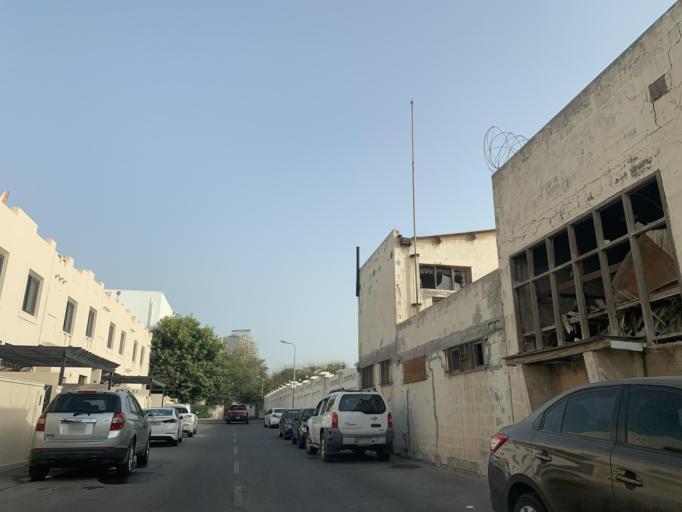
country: BH
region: Manama
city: Manama
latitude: 26.2080
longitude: 50.6018
